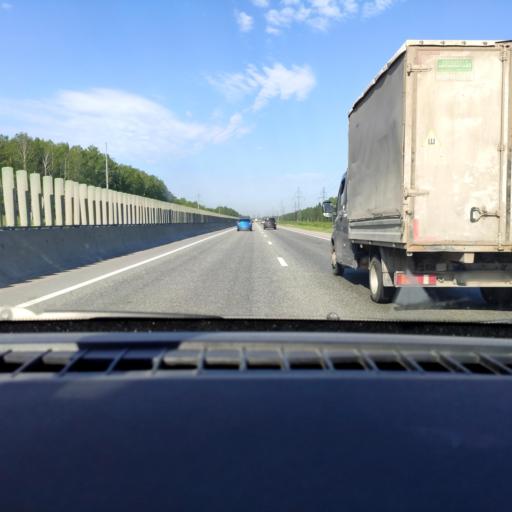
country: RU
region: Perm
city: Overyata
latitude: 58.0364
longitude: 55.9556
